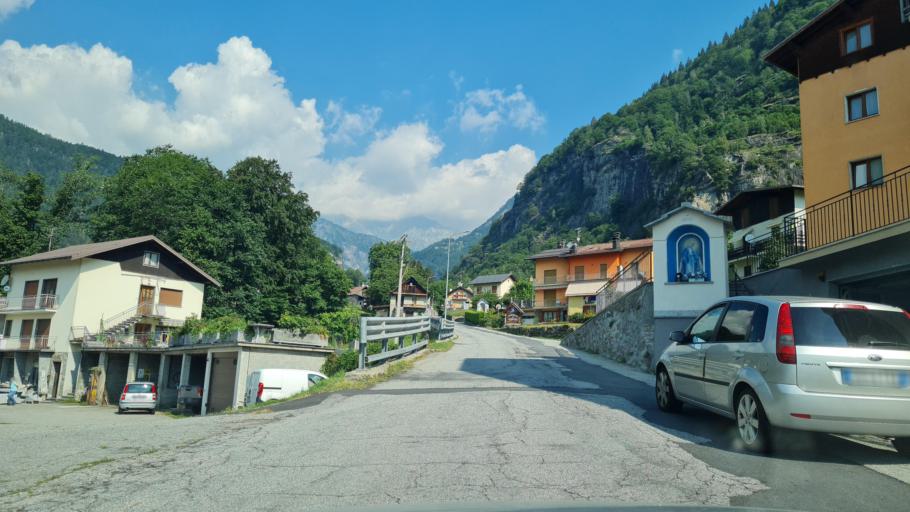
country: IT
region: Piedmont
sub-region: Provincia Verbano-Cusio-Ossola
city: Baceno
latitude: 46.2699
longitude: 8.3086
